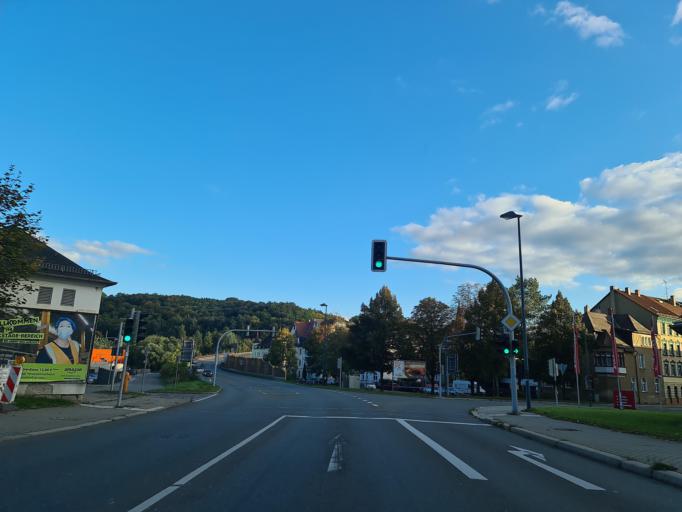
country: DE
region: Thuringia
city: Weida
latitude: 50.7800
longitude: 12.0640
